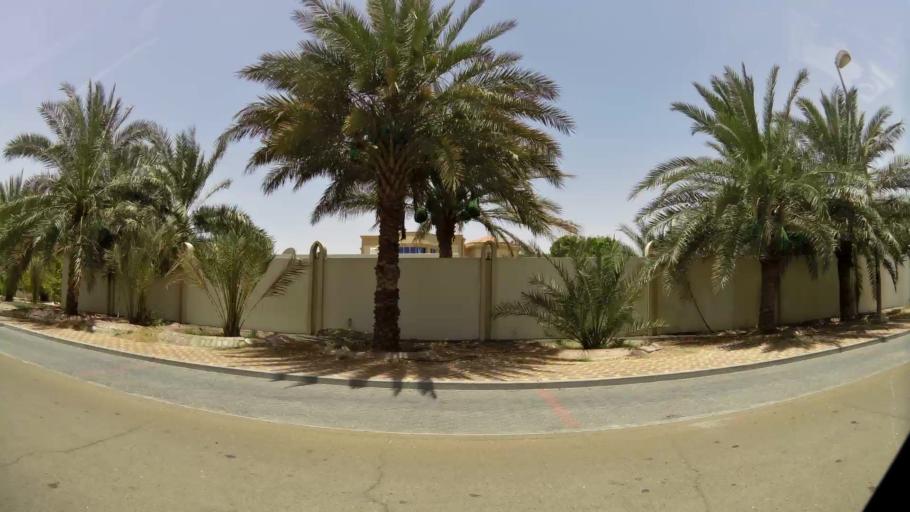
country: OM
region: Al Buraimi
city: Al Buraymi
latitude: 24.2802
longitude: 55.7329
